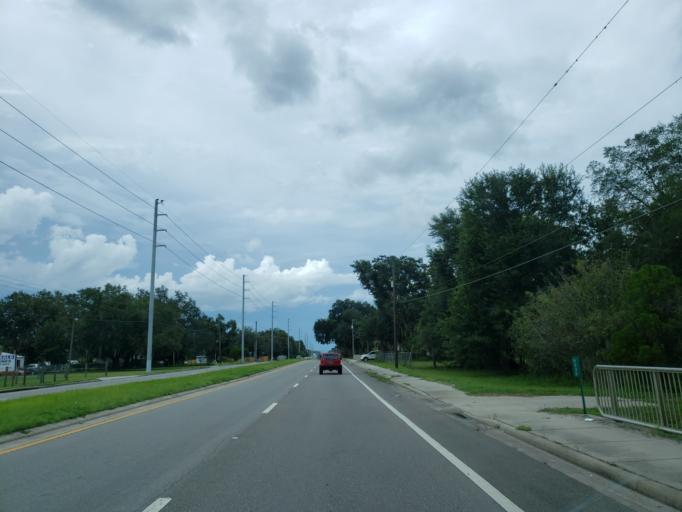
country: US
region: Florida
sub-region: Polk County
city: Willow Oak
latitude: 27.9454
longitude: -82.0552
